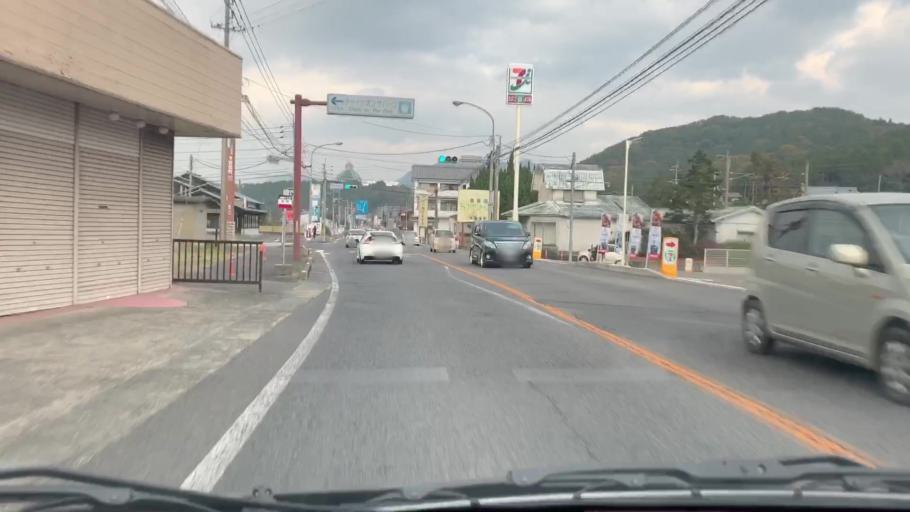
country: JP
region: Saga Prefecture
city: Imaricho-ko
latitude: 33.1806
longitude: 129.8528
